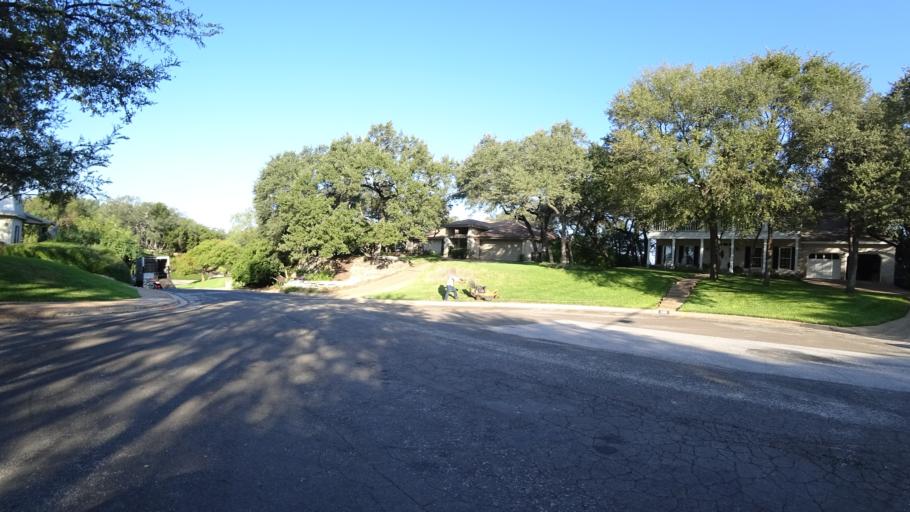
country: US
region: Texas
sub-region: Travis County
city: Rollingwood
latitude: 30.2634
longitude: -97.7978
